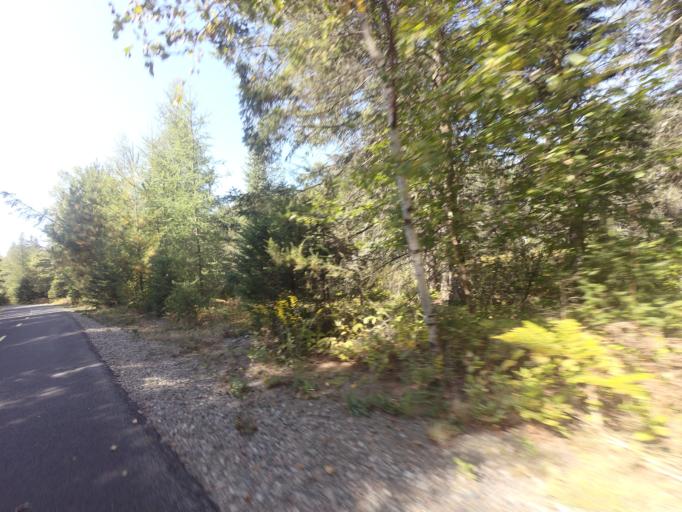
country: CA
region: Quebec
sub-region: Laurentides
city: Mont-Tremblant
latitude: 46.1294
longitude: -74.5522
